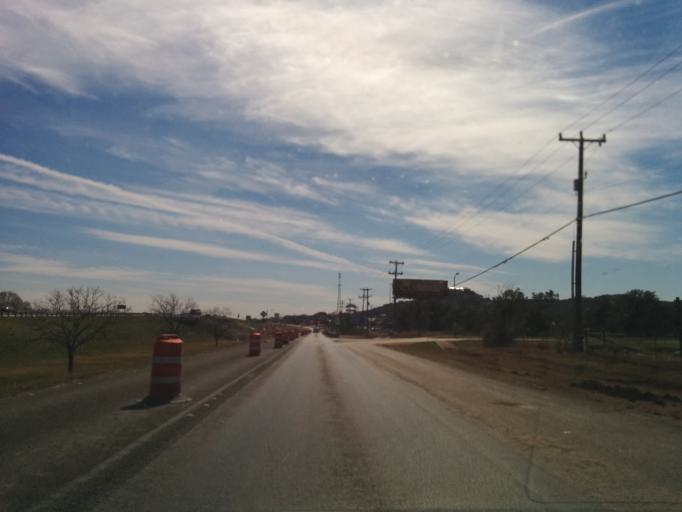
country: US
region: Texas
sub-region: Bexar County
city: Cross Mountain
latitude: 29.6690
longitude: -98.6333
